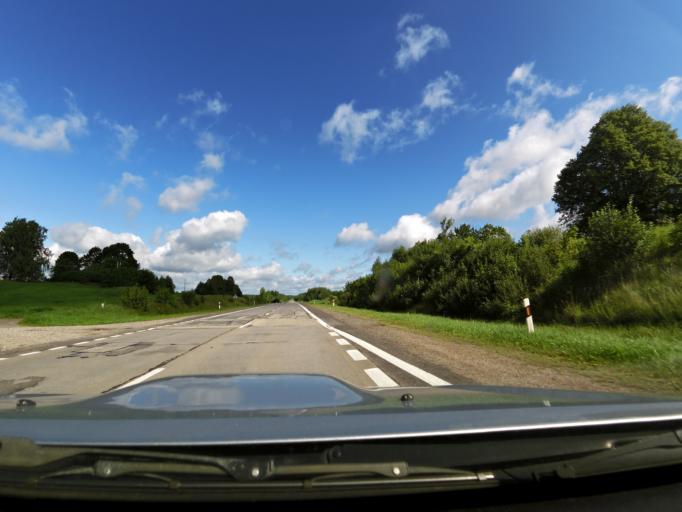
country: LT
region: Utenos apskritis
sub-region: Utena
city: Utena
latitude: 55.3816
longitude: 25.5200
